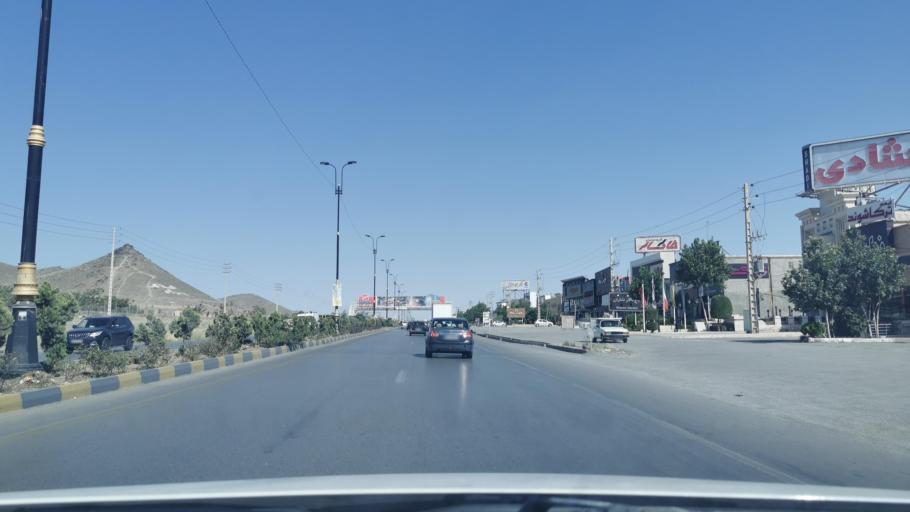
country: IR
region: Razavi Khorasan
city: Torqabeh
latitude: 36.3918
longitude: 59.4033
